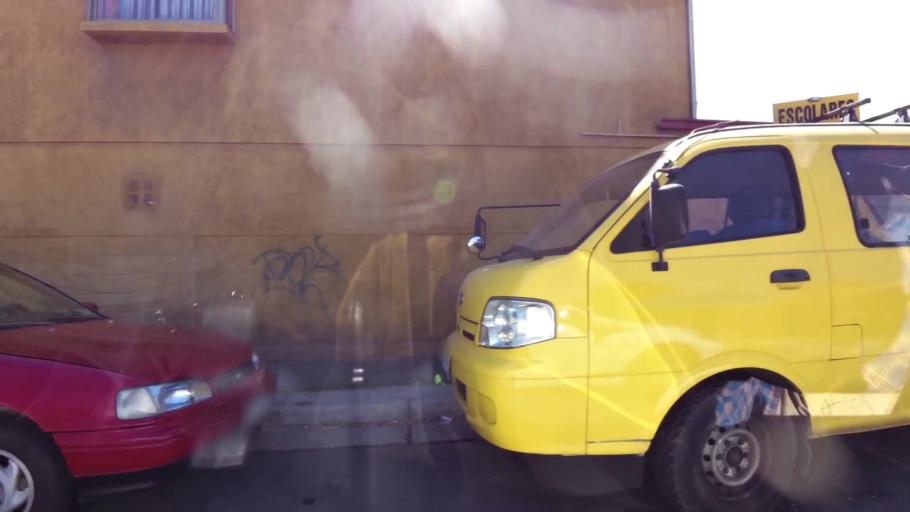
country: CL
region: O'Higgins
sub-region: Provincia de Cachapoal
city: Rancagua
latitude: -34.1682
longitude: -70.7628
